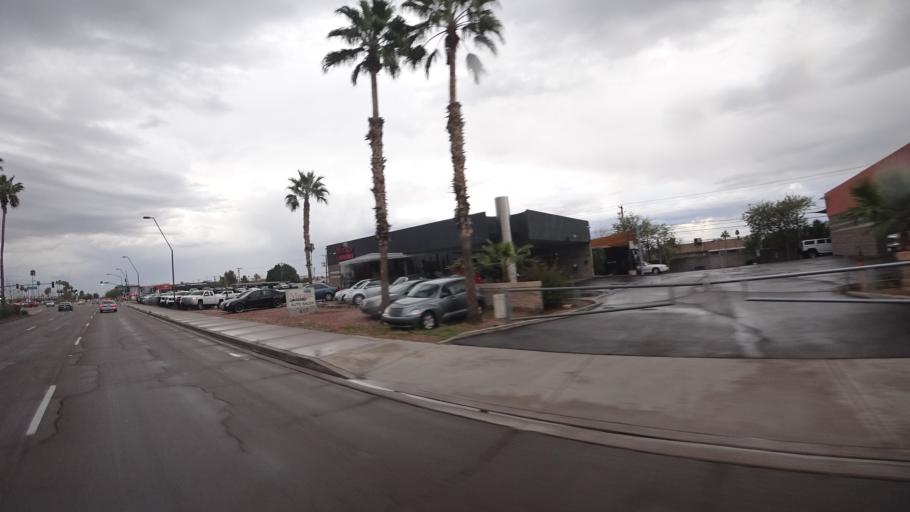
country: US
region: Arizona
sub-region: Maricopa County
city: Tempe
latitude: 33.4571
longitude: -111.9263
